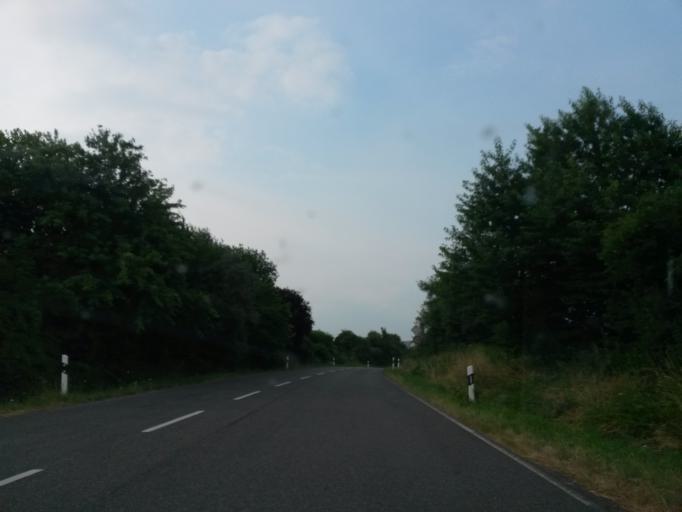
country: DE
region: North Rhine-Westphalia
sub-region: Regierungsbezirk Koln
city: Hennef
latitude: 50.7940
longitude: 7.3024
